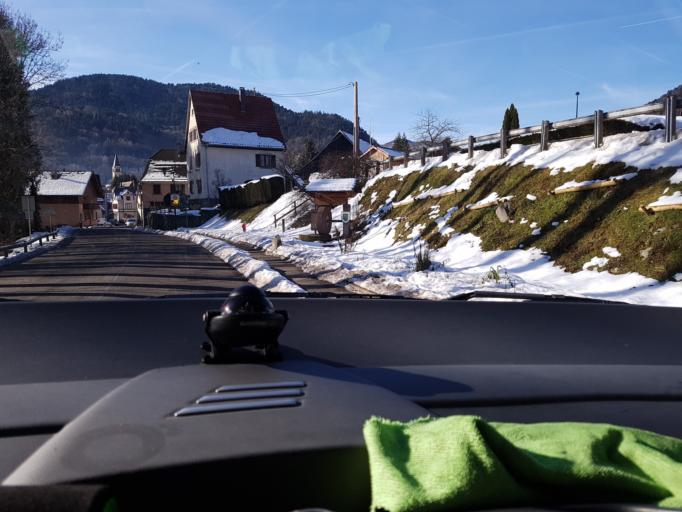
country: FR
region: Alsace
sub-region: Departement du Haut-Rhin
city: Metzeral
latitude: 48.0153
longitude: 7.0726
